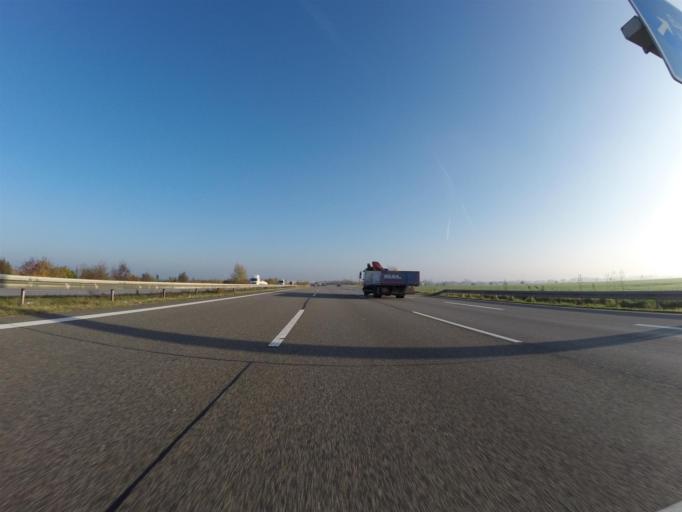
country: DE
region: Saxony-Anhalt
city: Kotzschau
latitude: 51.2862
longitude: 12.1308
